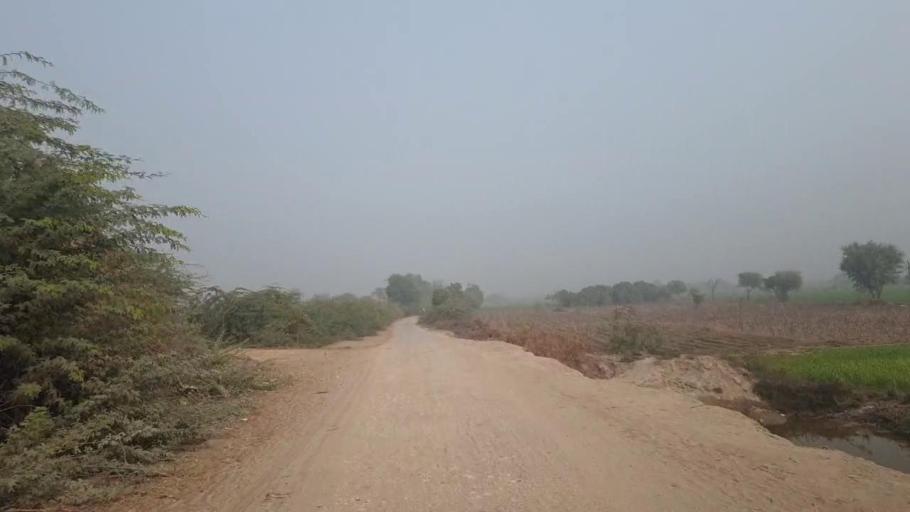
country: PK
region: Sindh
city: Bhit Shah
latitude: 25.8012
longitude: 68.5640
